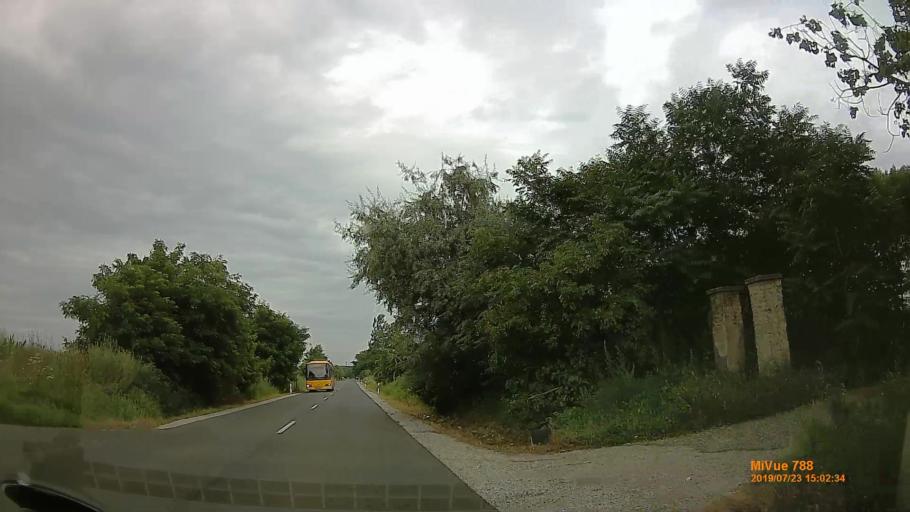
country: HU
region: Szabolcs-Szatmar-Bereg
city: Nyiregyhaza
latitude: 47.9318
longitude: 21.7005
